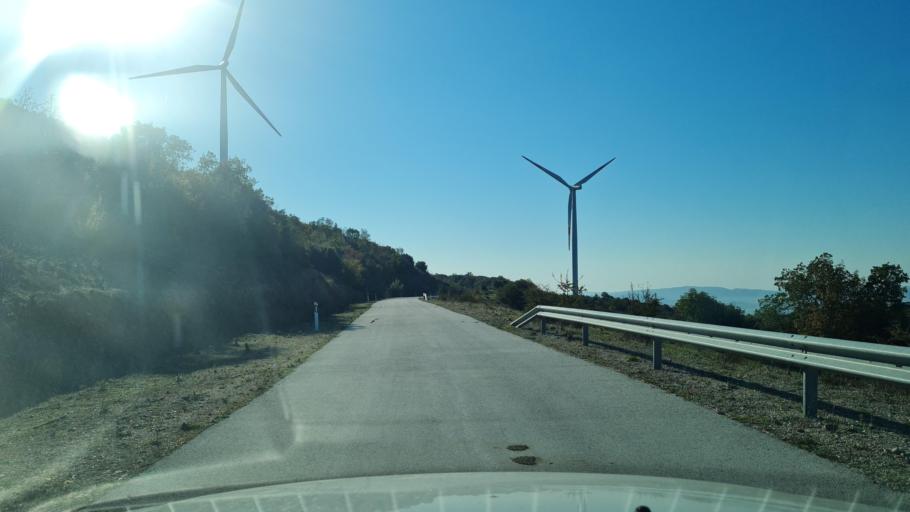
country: MK
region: Bogdanci
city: Bogdanci
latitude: 41.2270
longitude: 22.5525
